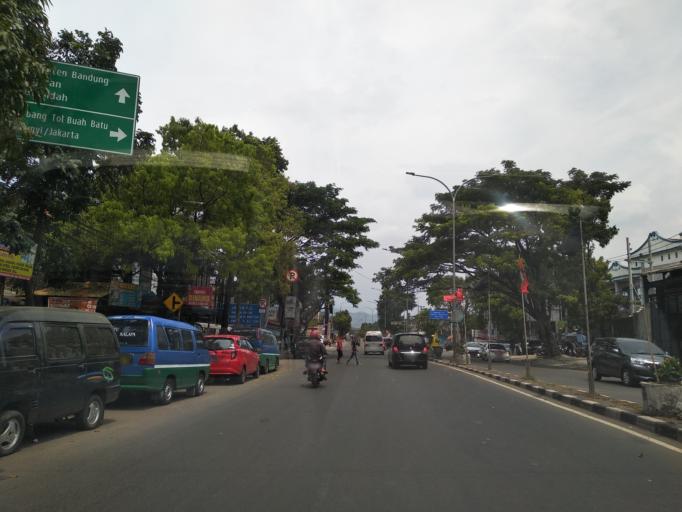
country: ID
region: West Java
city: Bandung
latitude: -6.9612
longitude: 107.6389
